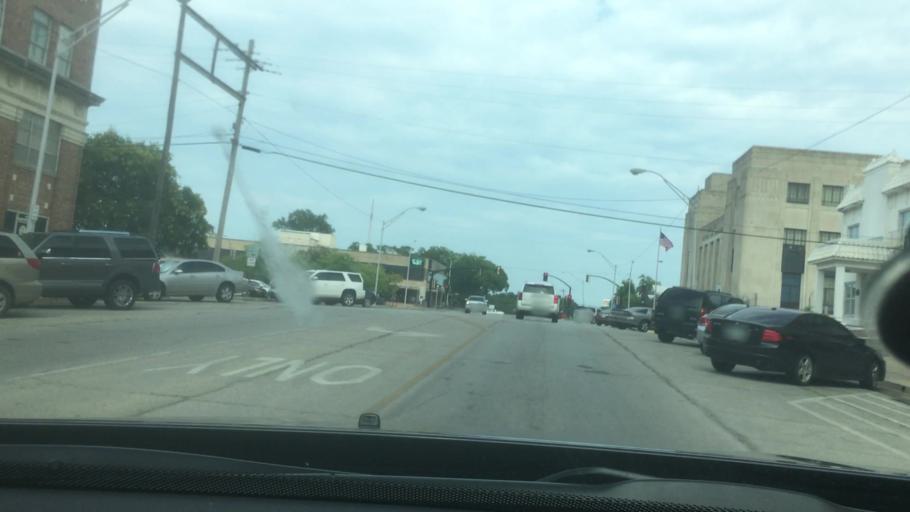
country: US
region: Oklahoma
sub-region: Pontotoc County
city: Ada
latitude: 34.7734
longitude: -96.6785
